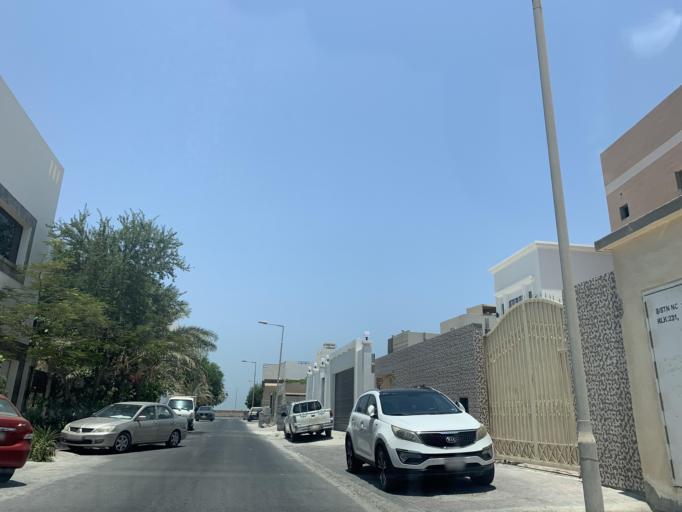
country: BH
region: Muharraq
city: Al Muharraq
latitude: 26.2832
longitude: 50.6186
